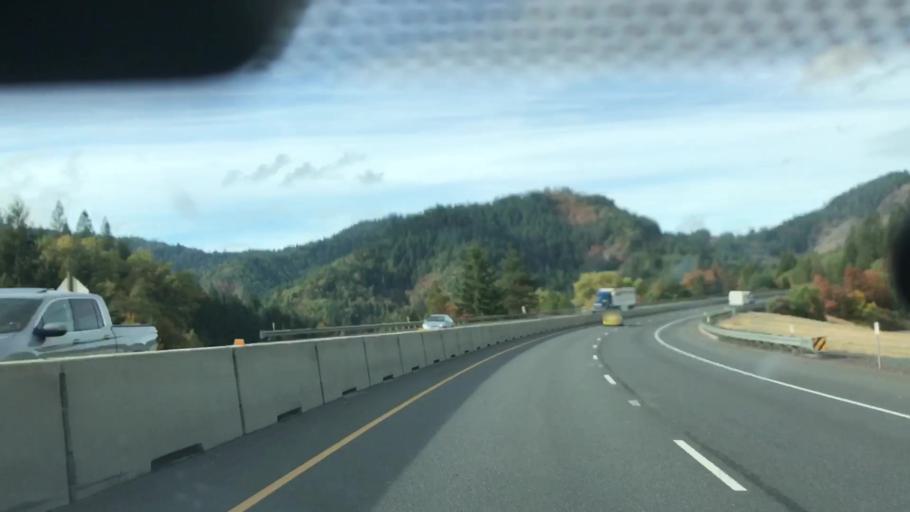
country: US
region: Oregon
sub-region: Josephine County
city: Merlin
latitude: 42.6887
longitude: -123.3931
